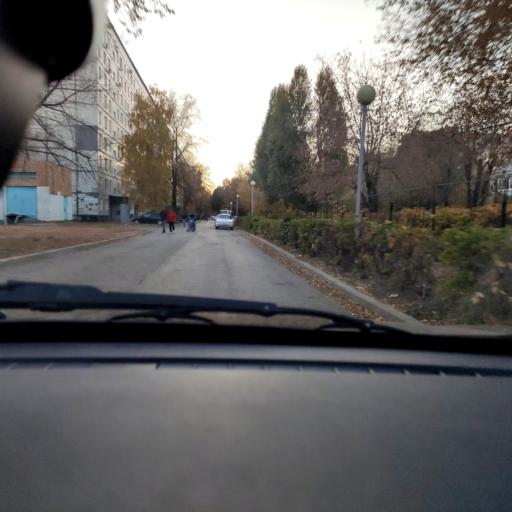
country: RU
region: Samara
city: Tol'yatti
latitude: 53.5365
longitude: 49.2718
